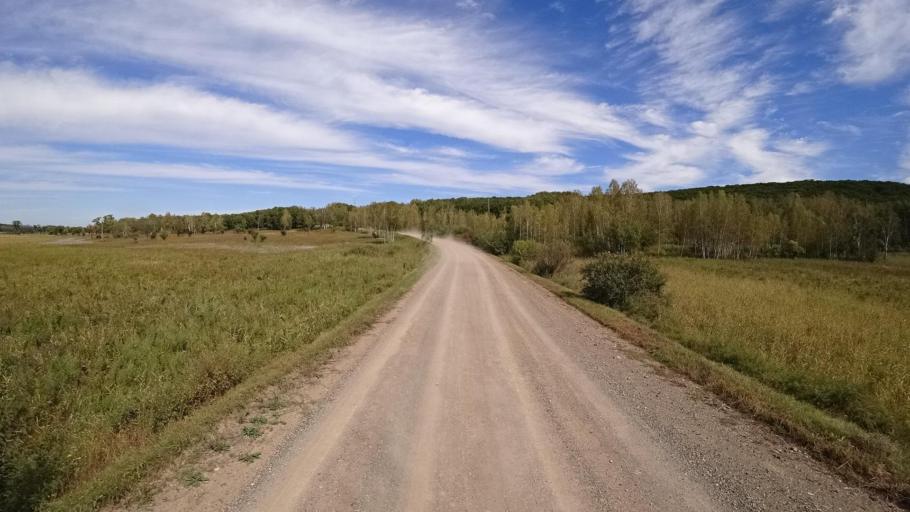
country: RU
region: Primorskiy
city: Yakovlevka
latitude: 44.6789
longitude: 133.6155
